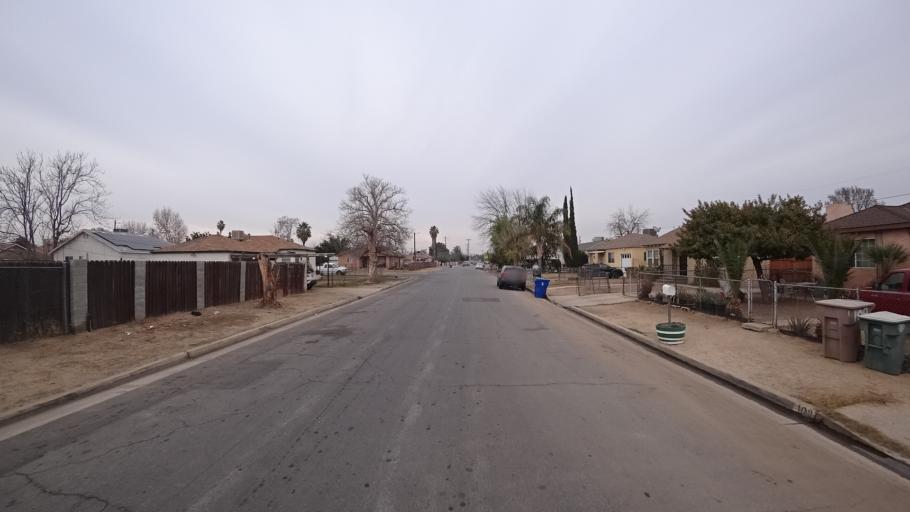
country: US
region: California
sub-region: Kern County
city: Bakersfield
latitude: 35.3561
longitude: -118.9991
